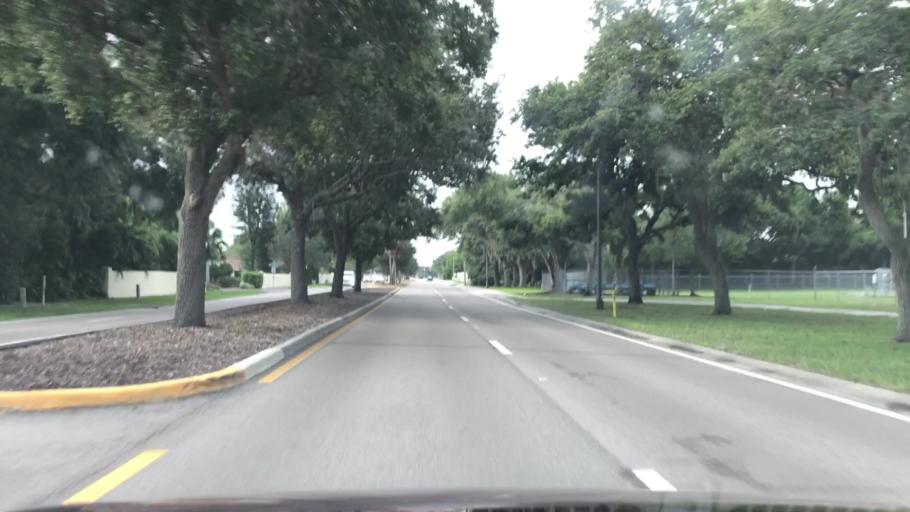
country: US
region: Florida
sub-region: Sarasota County
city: Plantation
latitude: 27.0748
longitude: -82.3888
